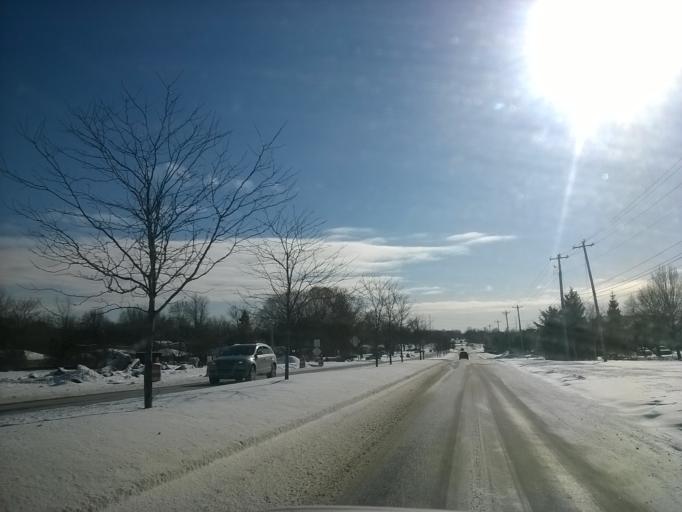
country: US
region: Indiana
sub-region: Hamilton County
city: Carmel
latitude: 39.9314
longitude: -86.1269
